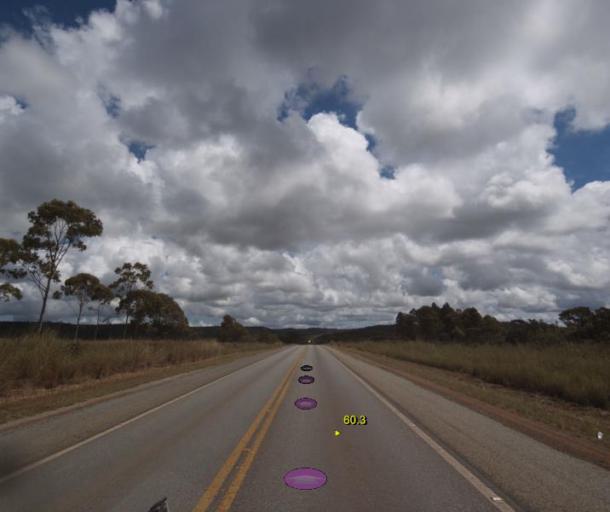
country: BR
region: Goias
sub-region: Pirenopolis
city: Pirenopolis
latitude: -15.7658
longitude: -48.7088
